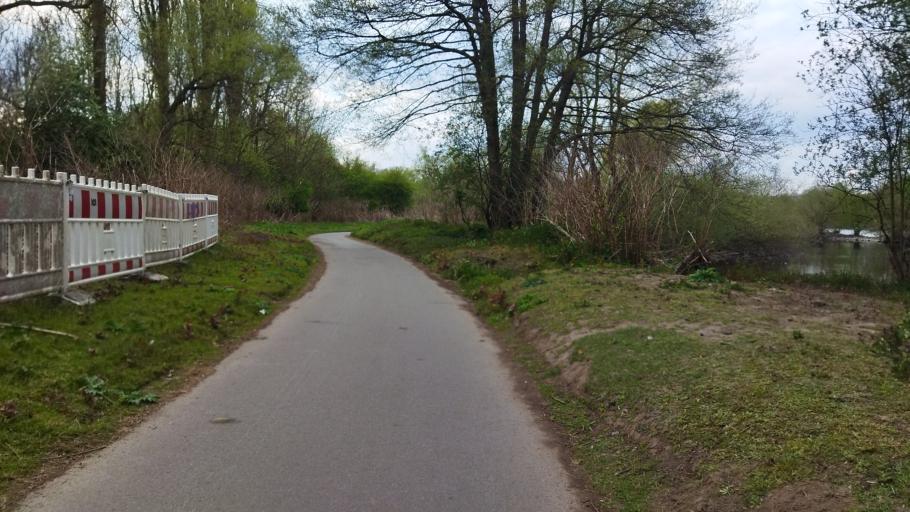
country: DE
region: North Rhine-Westphalia
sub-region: Regierungsbezirk Dusseldorf
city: Essen
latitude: 51.4208
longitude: 7.0657
